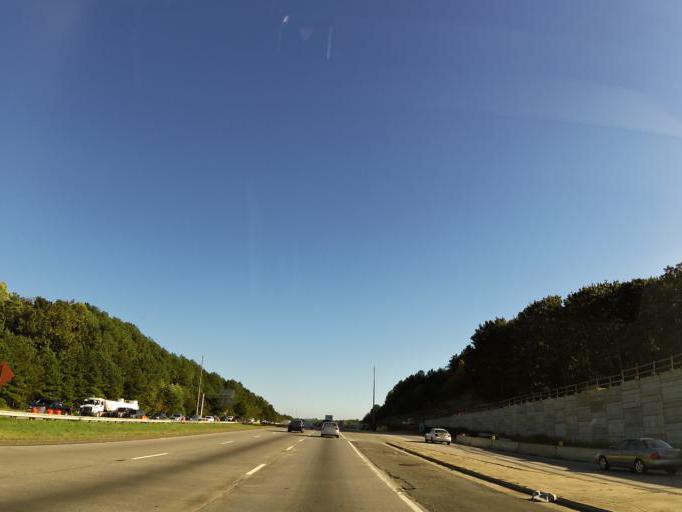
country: US
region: Georgia
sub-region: Cobb County
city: Kennesaw
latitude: 34.0064
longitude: -84.5660
